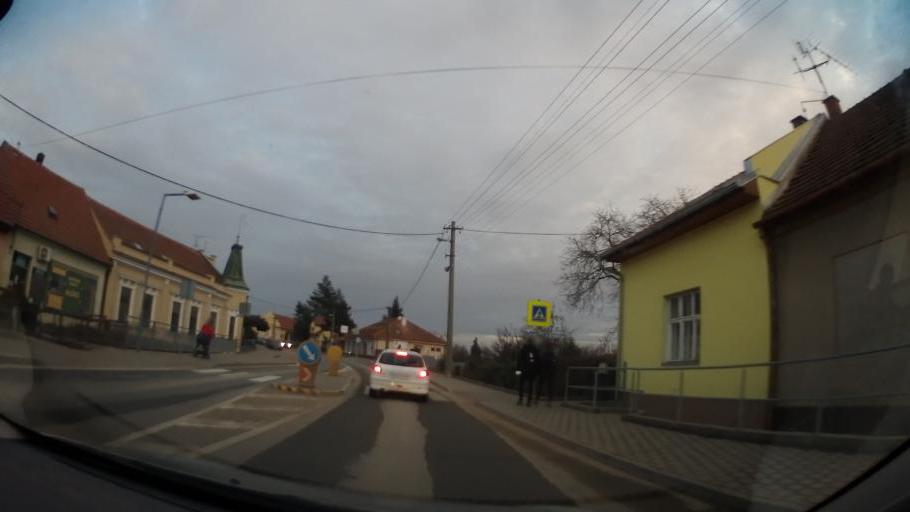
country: CZ
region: South Moravian
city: Troubsko
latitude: 49.1757
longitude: 16.5203
